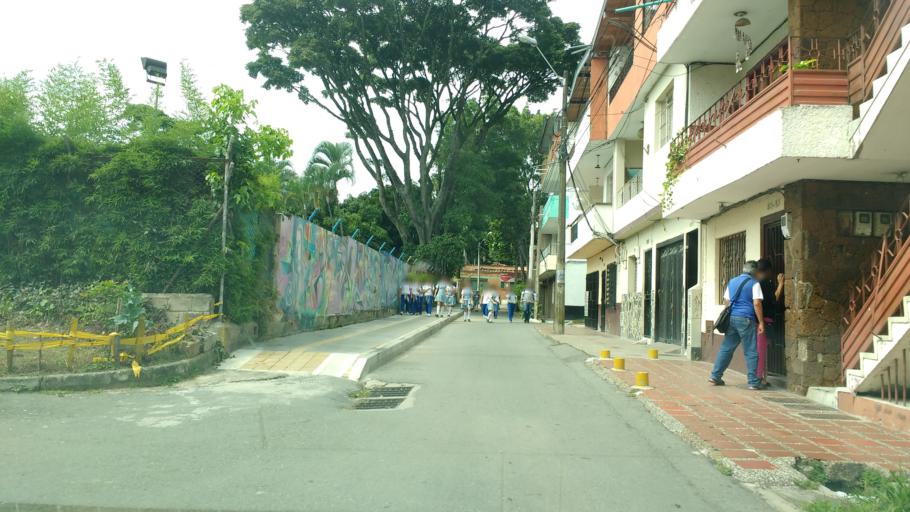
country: CO
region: Antioquia
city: Medellin
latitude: 6.2600
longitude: -75.6058
